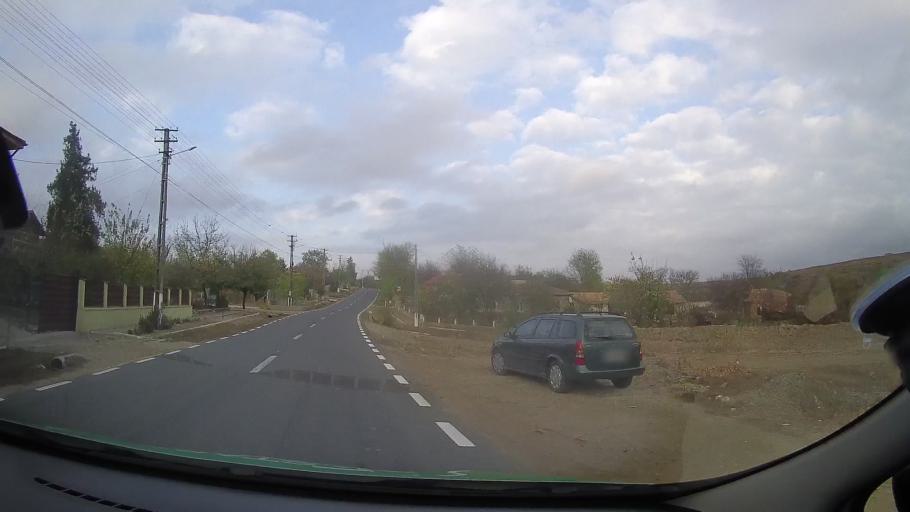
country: RO
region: Constanta
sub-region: Comuna Mircea Voda
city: Mircea Voda
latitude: 44.2767
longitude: 28.1726
